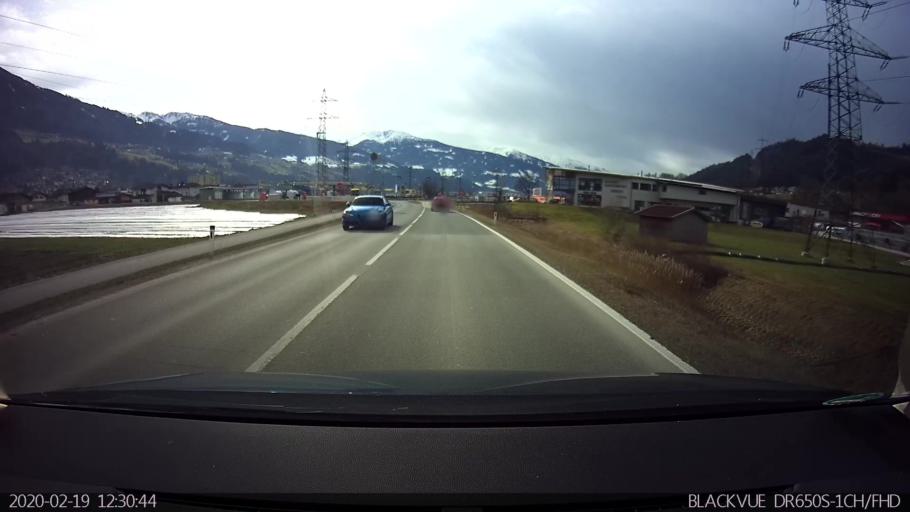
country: AT
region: Tyrol
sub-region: Politischer Bezirk Schwaz
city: Schwaz
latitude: 47.3544
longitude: 11.7008
